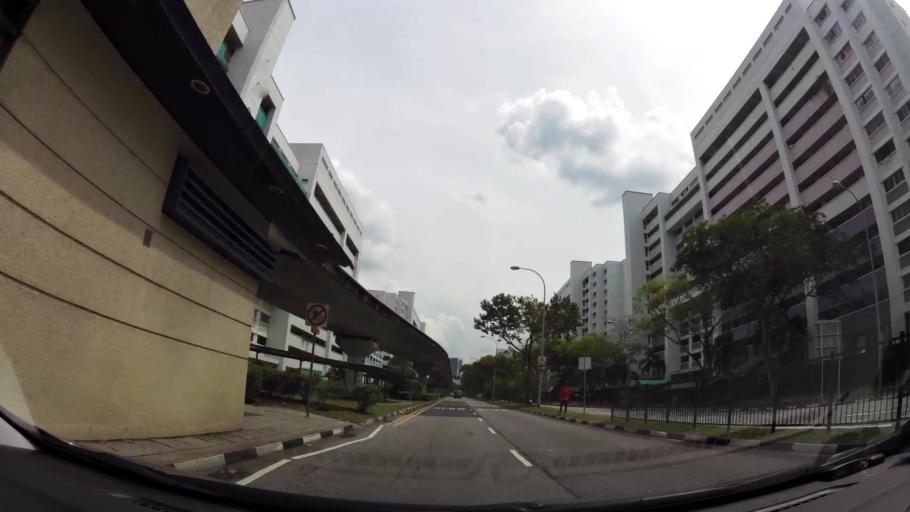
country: MY
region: Johor
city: Johor Bahru
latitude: 1.3776
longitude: 103.7666
